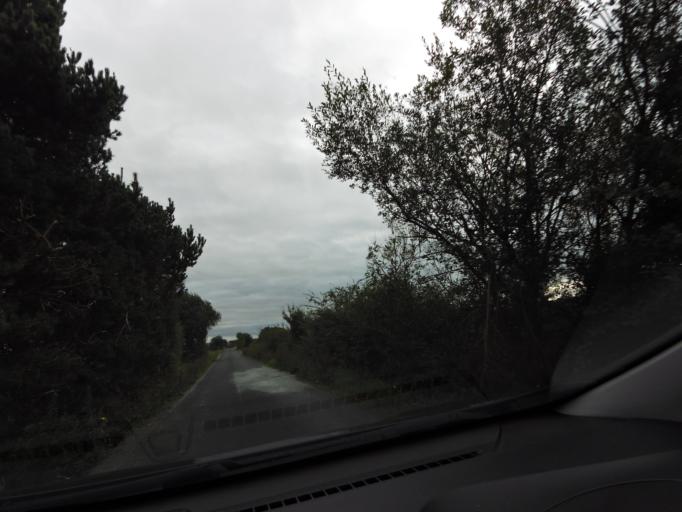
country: IE
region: Leinster
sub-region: Uibh Fhaili
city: Ferbane
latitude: 53.2161
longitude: -7.7256
